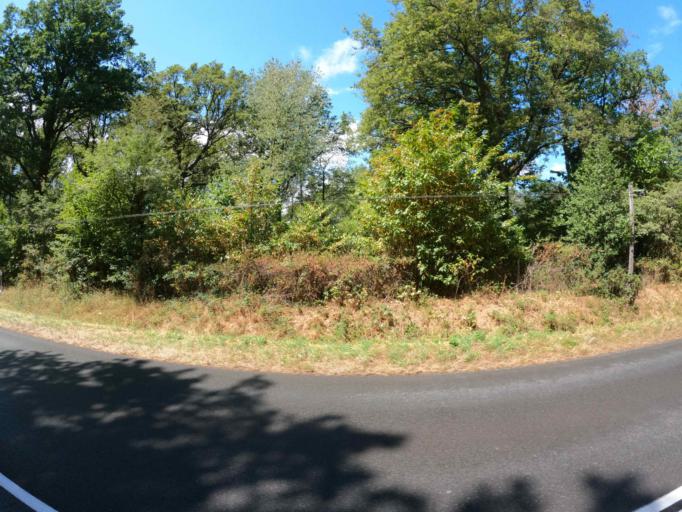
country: FR
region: Pays de la Loire
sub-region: Departement de Maine-et-Loire
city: Champigne
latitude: 47.6288
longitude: -0.5813
